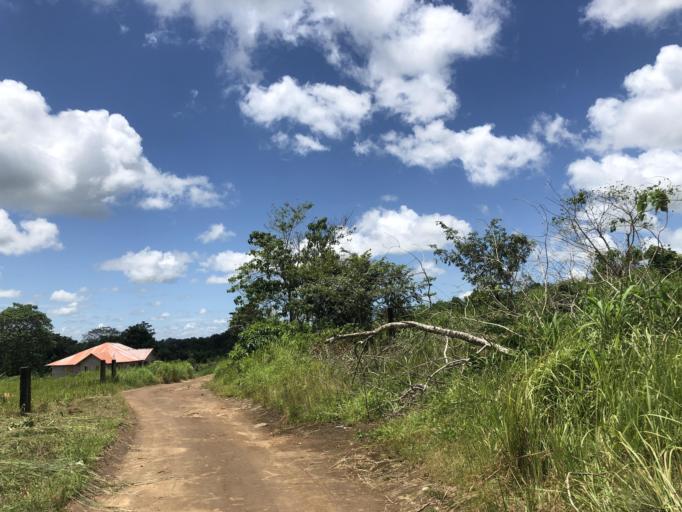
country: SL
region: Northern Province
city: Makeni
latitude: 8.8494
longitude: -12.0609
